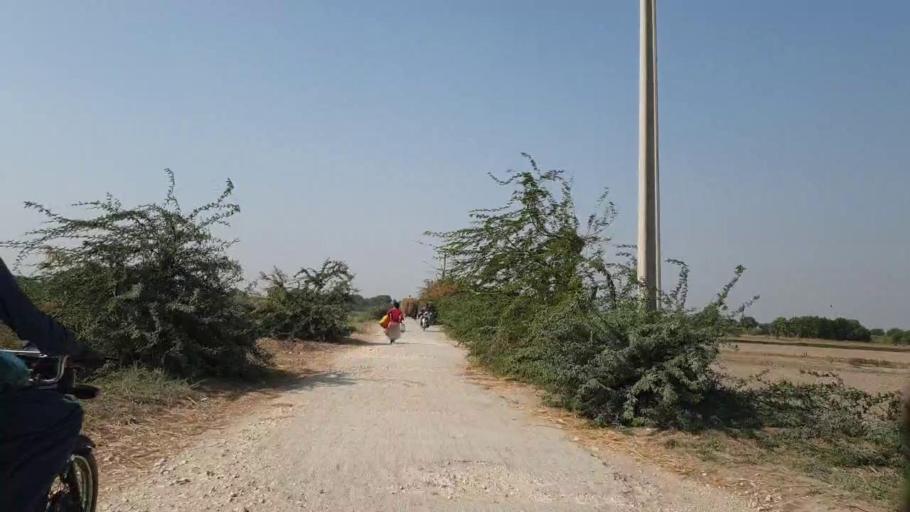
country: PK
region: Sindh
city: Bulri
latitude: 24.9578
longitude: 68.3333
